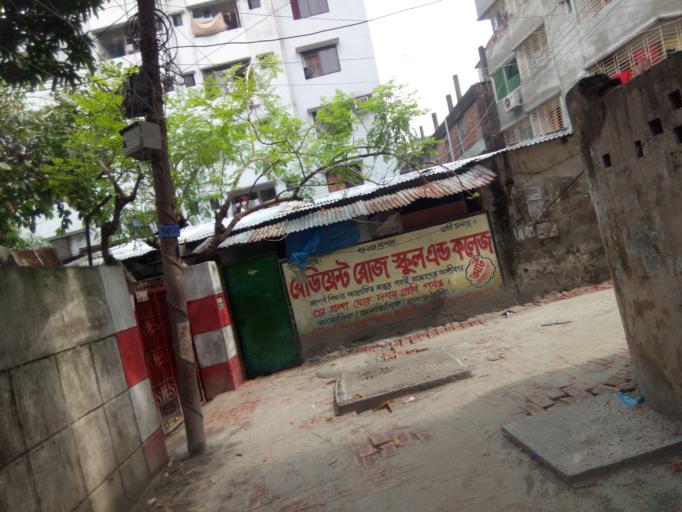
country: BD
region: Dhaka
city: Azimpur
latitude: 23.7416
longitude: 90.3708
